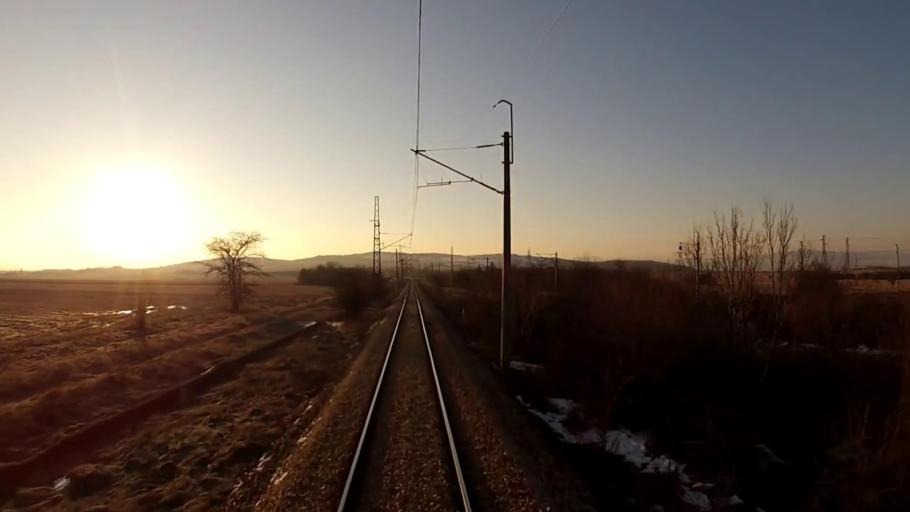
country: BG
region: Sofiya
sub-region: Obshtina Slivnitsa
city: Slivnitsa
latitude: 42.8803
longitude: 22.9988
